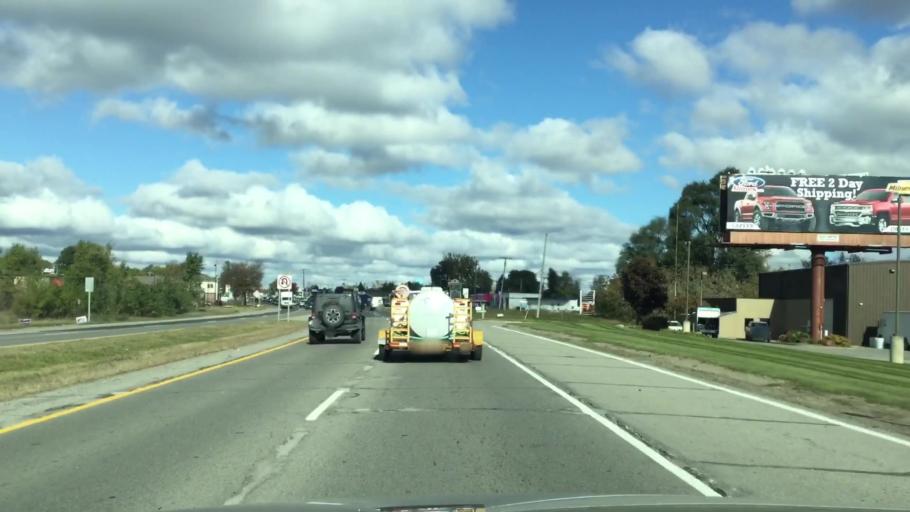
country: US
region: Michigan
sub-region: Oakland County
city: Lake Orion
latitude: 42.8064
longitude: -83.2485
